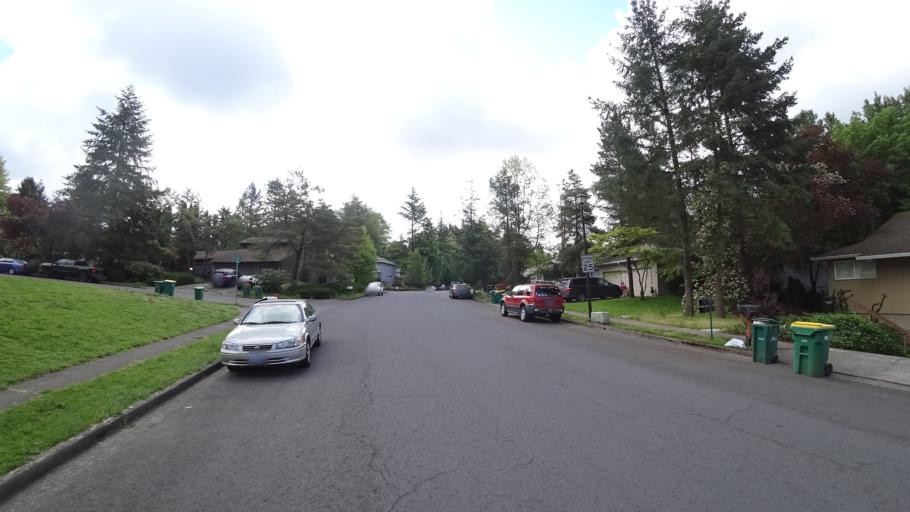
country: US
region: Oregon
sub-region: Washington County
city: Beaverton
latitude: 45.4695
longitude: -122.8257
